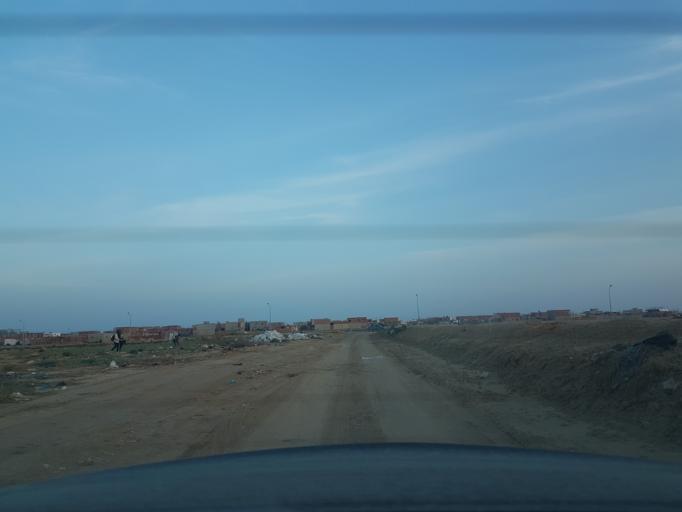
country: TN
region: Safaqis
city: Sfax
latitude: 34.7026
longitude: 10.6975
